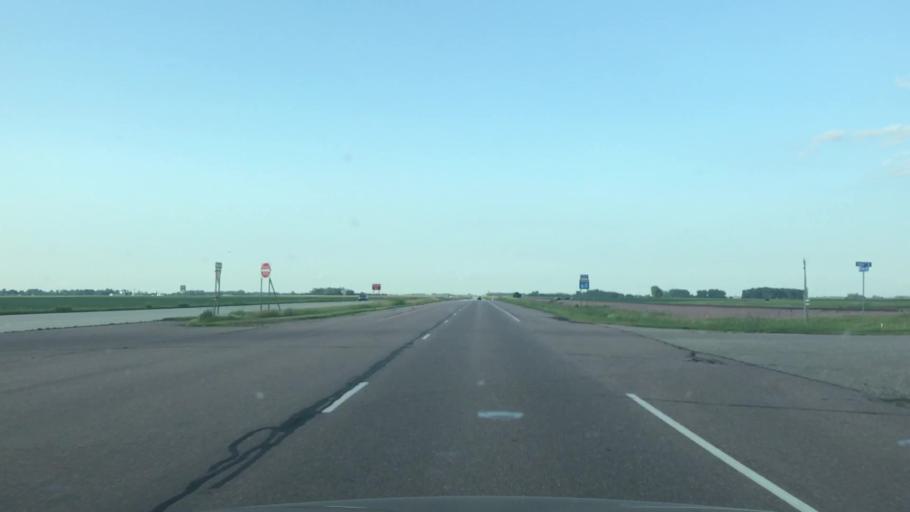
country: US
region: Minnesota
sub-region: Nobles County
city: Worthington
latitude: 43.7318
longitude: -95.4203
